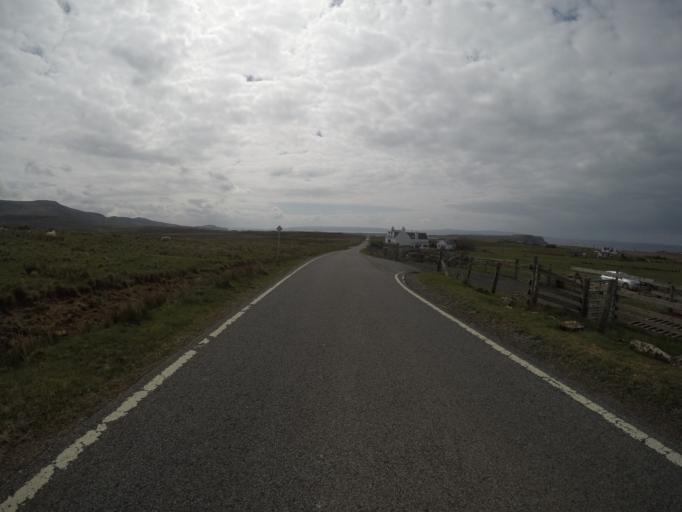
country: GB
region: Scotland
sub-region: Highland
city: Portree
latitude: 57.6581
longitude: -6.3741
